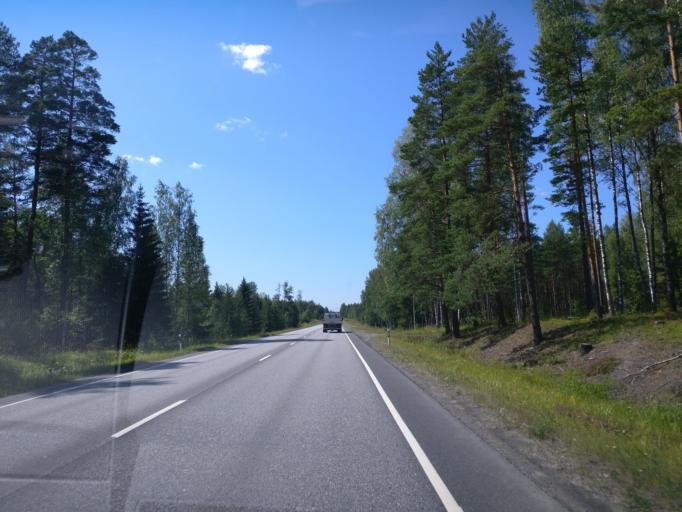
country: FI
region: Satakunta
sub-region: Pori
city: Kullaa
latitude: 61.4600
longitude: 22.0939
